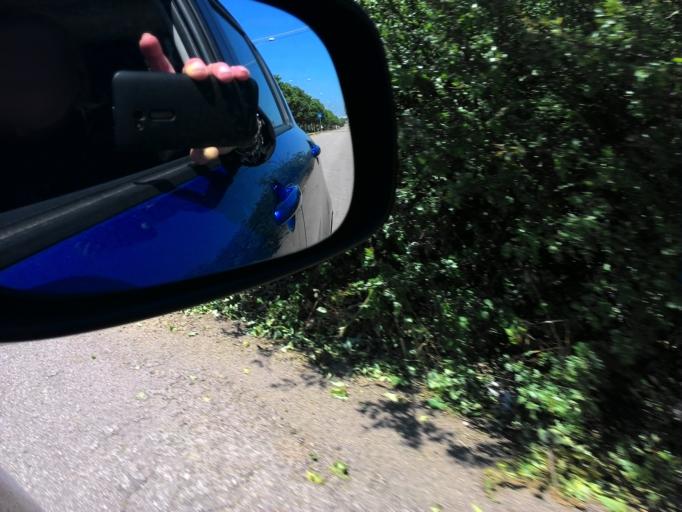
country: IT
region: Apulia
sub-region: Provincia di Bari
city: Putignano
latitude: 40.8488
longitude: 17.1401
